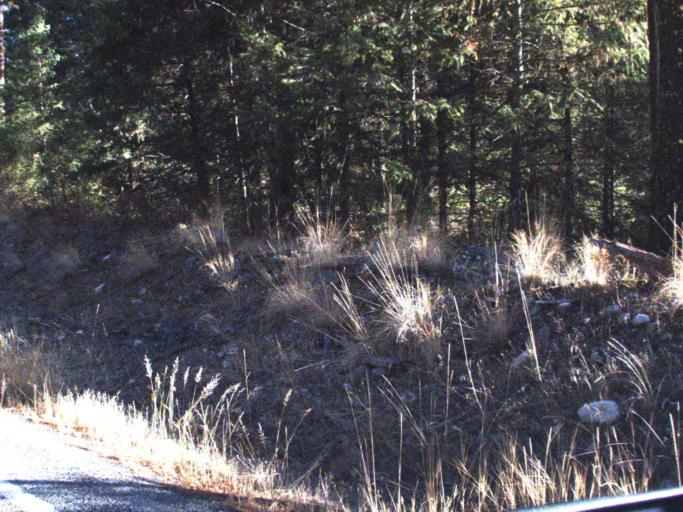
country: US
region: Washington
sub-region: Ferry County
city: Republic
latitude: 48.3744
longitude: -118.7493
